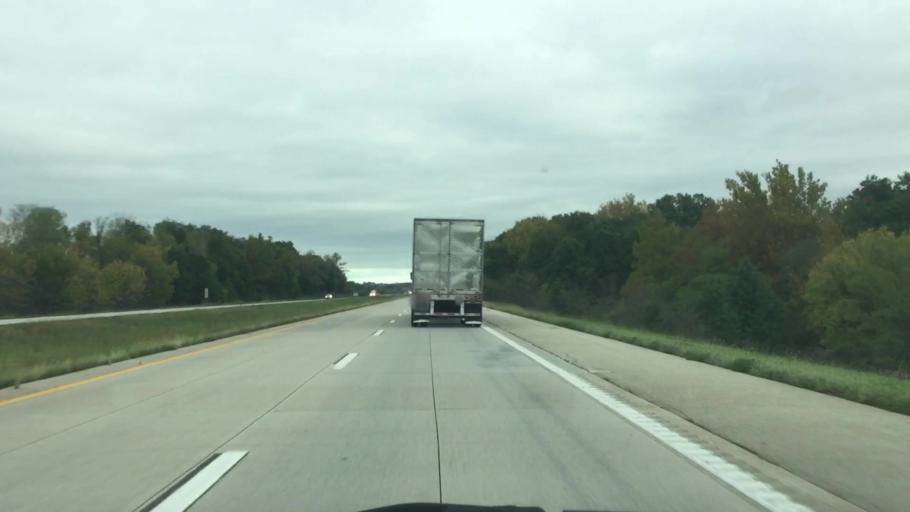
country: US
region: Missouri
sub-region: Daviess County
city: Gallatin
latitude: 40.0169
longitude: -94.0959
